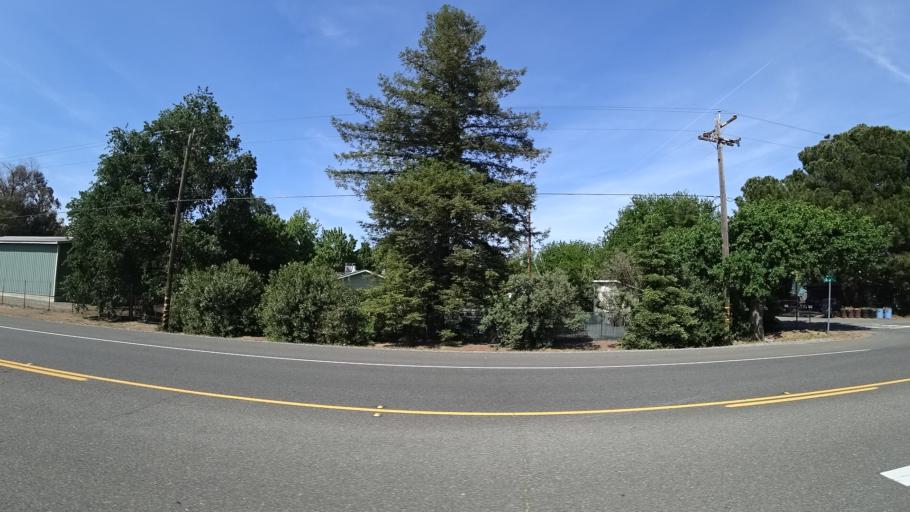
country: US
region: California
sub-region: Tehama County
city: Red Bluff
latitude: 40.1850
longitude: -122.1789
